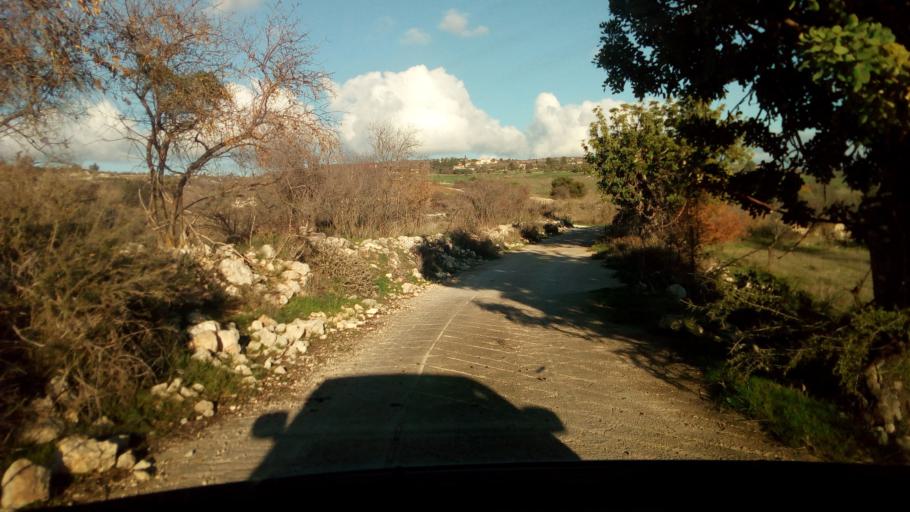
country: CY
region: Pafos
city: Tala
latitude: 34.9123
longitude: 32.5177
